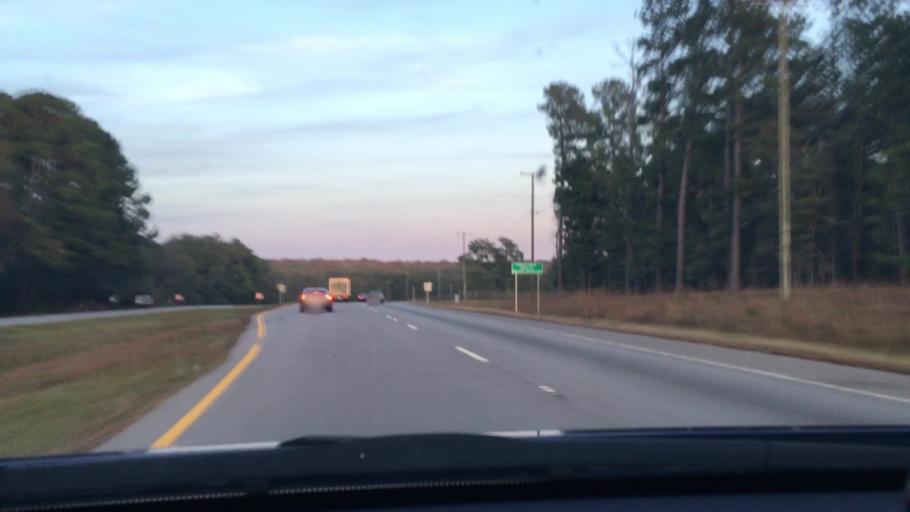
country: US
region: South Carolina
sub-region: Richland County
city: Gadsden
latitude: 33.9442
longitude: -80.7653
